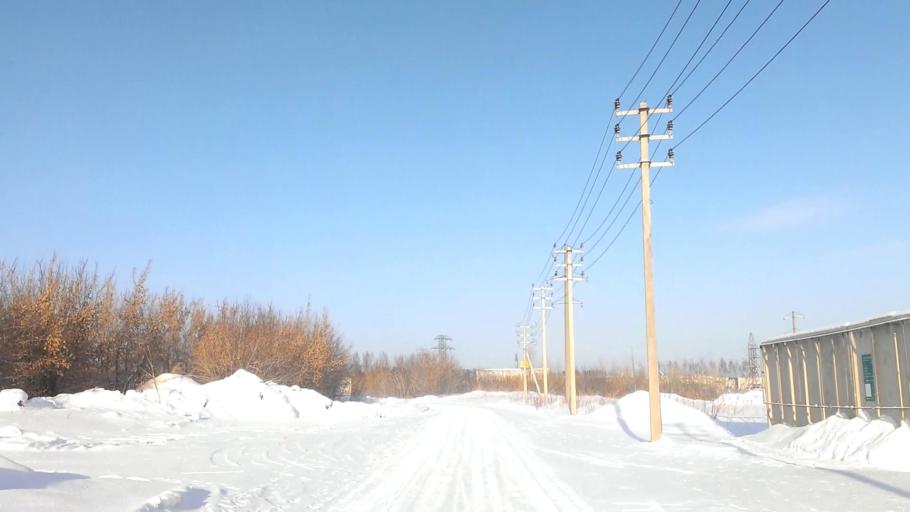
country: RU
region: Altai Krai
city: Novosilikatnyy
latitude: 53.3442
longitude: 83.6299
